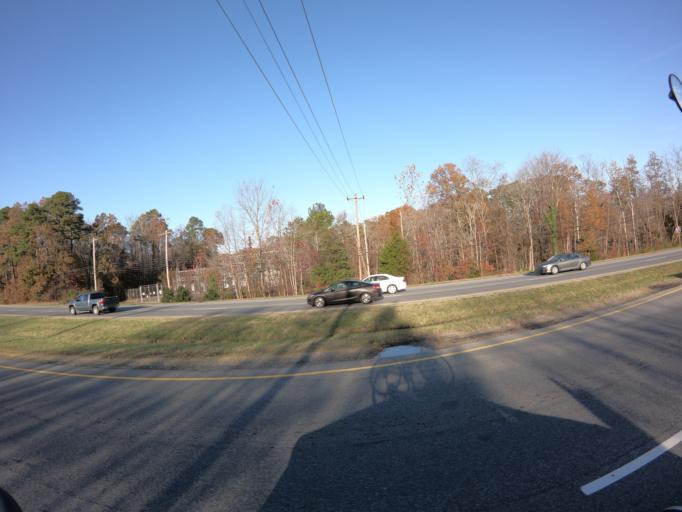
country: US
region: Maryland
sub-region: Saint Mary's County
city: Leonardtown
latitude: 38.3058
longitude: -76.6594
